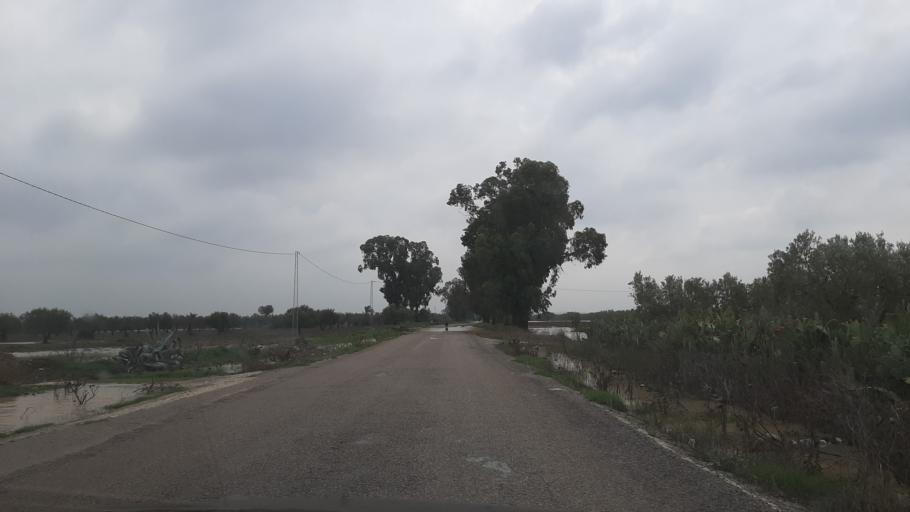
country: TN
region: Al Munastir
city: Sidi Bin Nur
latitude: 35.4521
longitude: 10.9056
